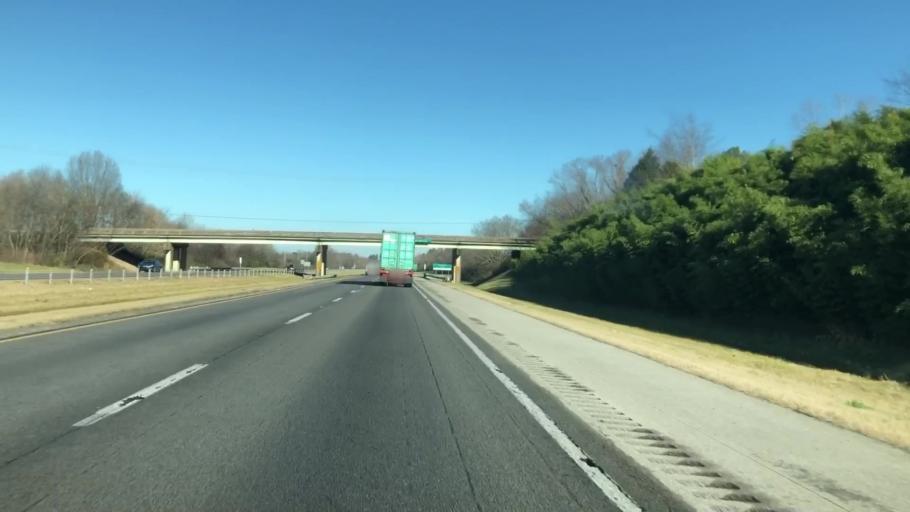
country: US
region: Alabama
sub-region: Limestone County
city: Athens
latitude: 34.8100
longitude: -86.9386
